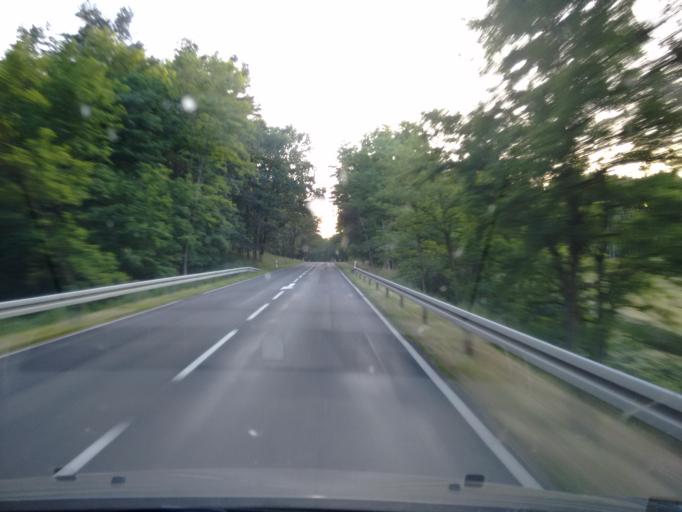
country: DE
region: Brandenburg
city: Mixdorf
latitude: 52.1385
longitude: 14.4792
